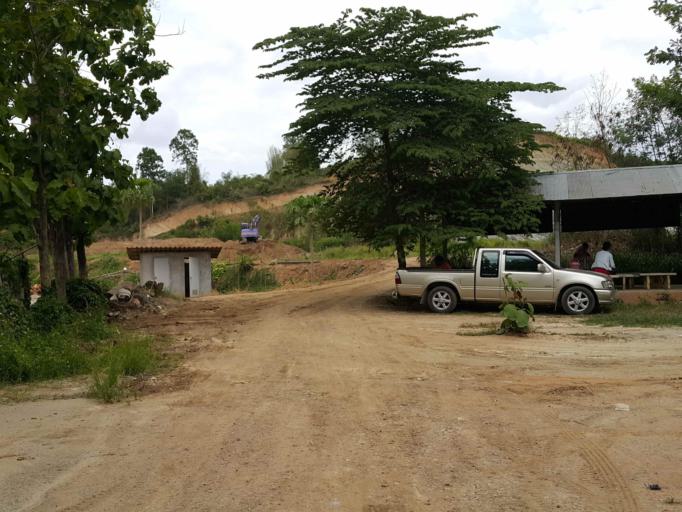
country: TH
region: Chiang Mai
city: Hang Dong
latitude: 18.7473
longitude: 98.8859
